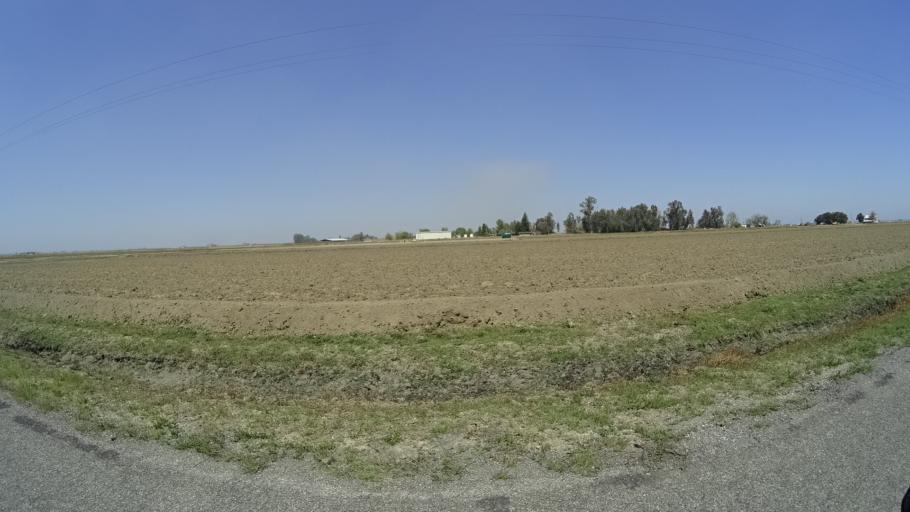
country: US
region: California
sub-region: Glenn County
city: Willows
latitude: 39.5435
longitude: -122.1022
